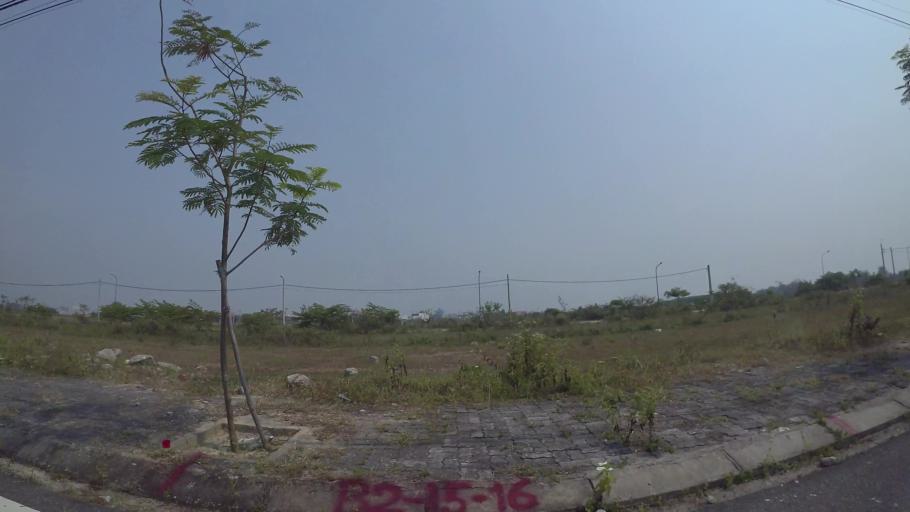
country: VN
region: Da Nang
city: Cam Le
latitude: 15.9713
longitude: 108.2130
